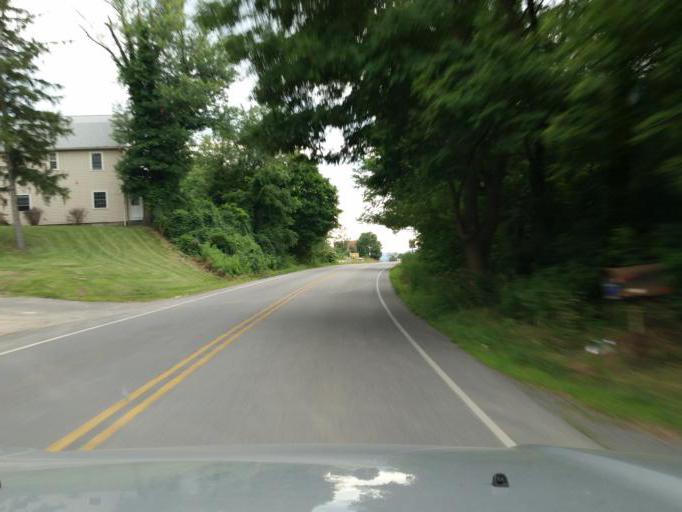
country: US
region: Pennsylvania
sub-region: Blair County
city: Altoona
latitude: 40.5300
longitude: -78.3793
